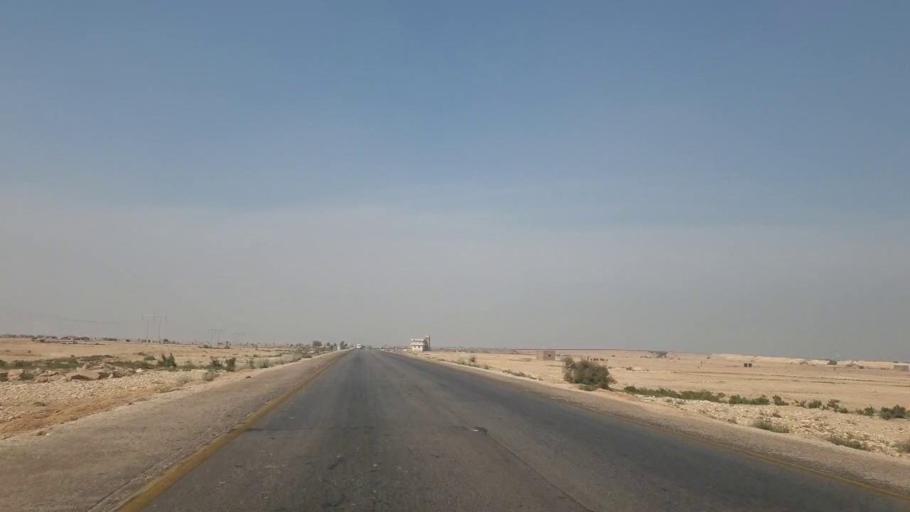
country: PK
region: Sindh
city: Hala
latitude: 25.8505
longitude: 68.2596
